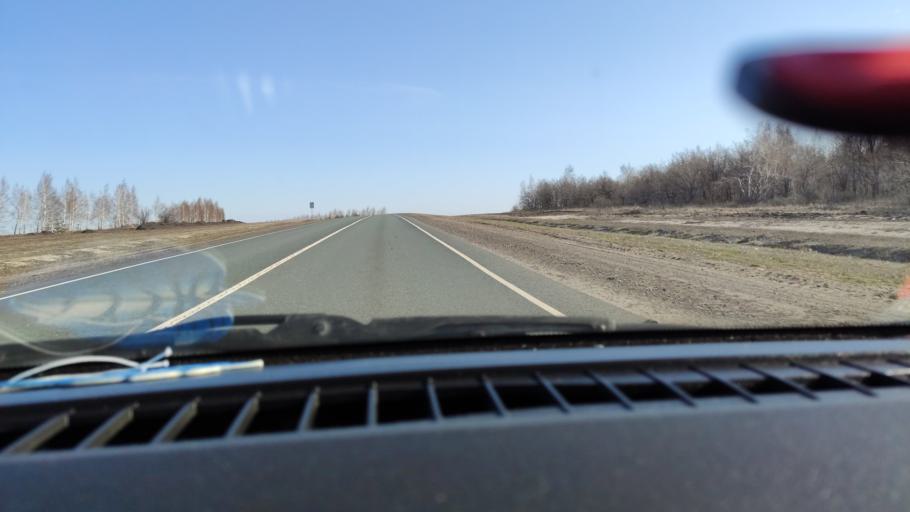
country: RU
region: Samara
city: Syzran'
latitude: 52.9322
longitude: 48.3072
